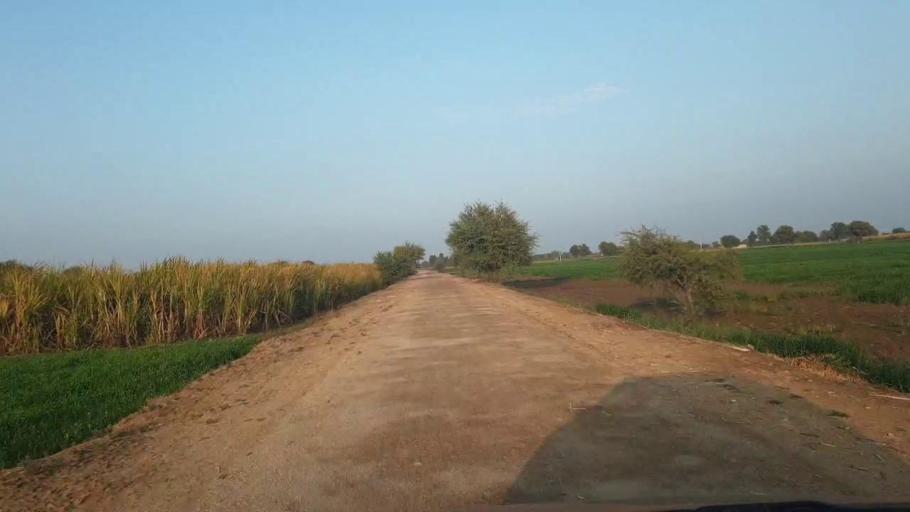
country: PK
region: Sindh
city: Berani
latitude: 25.8374
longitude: 68.7274
